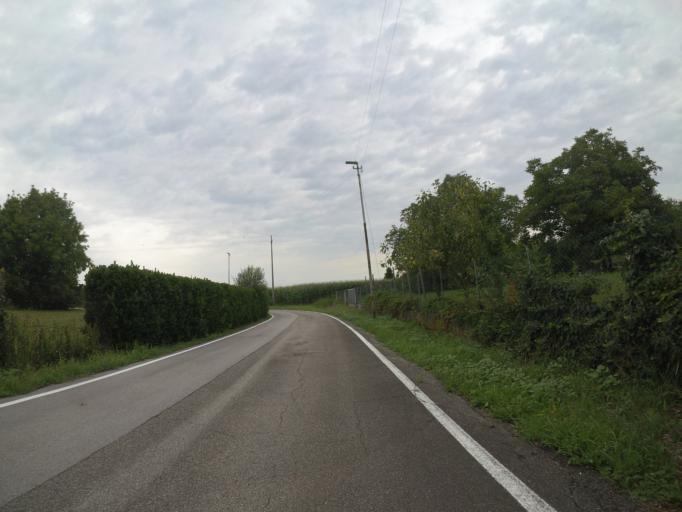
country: IT
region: Friuli Venezia Giulia
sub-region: Provincia di Udine
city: Varmo
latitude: 45.8781
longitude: 13.0073
